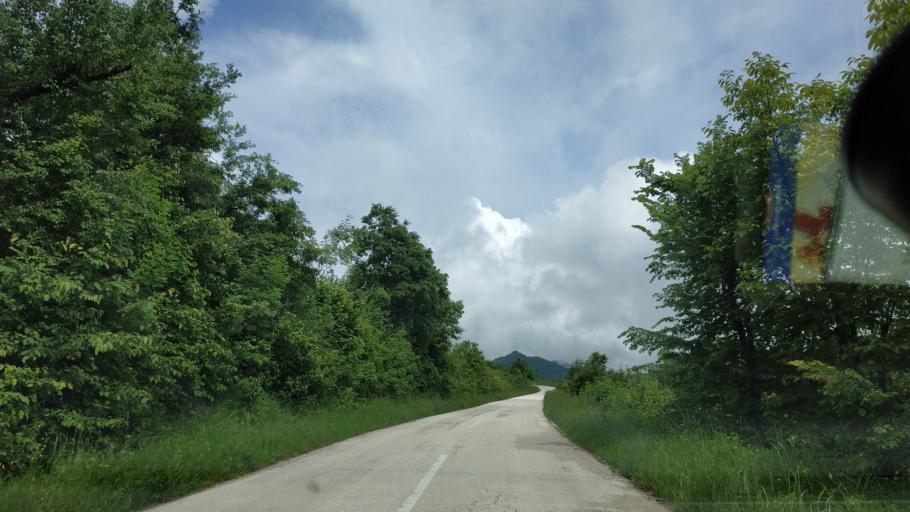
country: RS
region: Central Serbia
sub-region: Zajecarski Okrug
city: Boljevac
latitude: 43.7460
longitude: 21.9471
